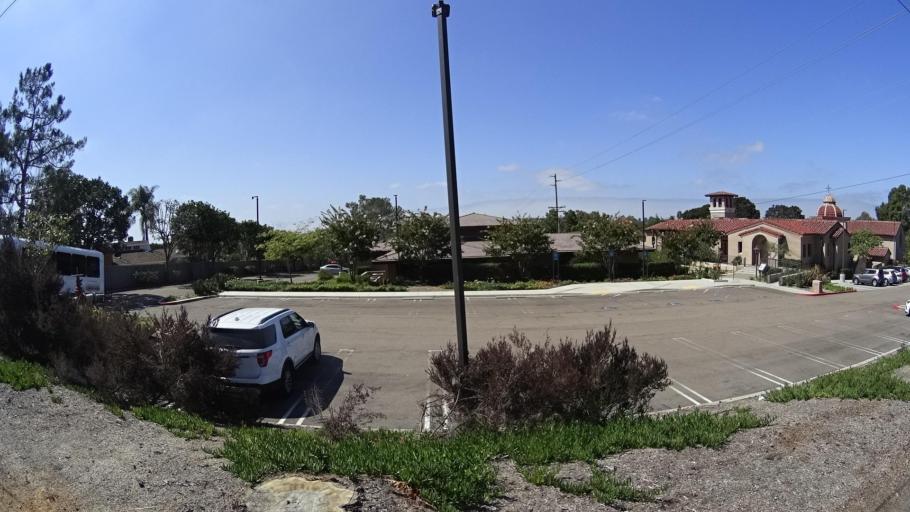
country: US
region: California
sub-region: San Diego County
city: Rancho Santa Fe
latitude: 33.0238
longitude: -117.1967
